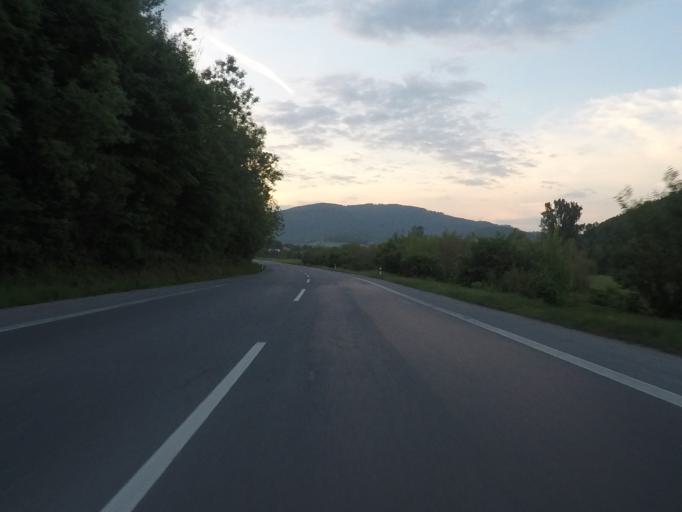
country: SK
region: Banskobystricky
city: Rimavska Sobota
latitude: 48.4940
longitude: 19.9404
